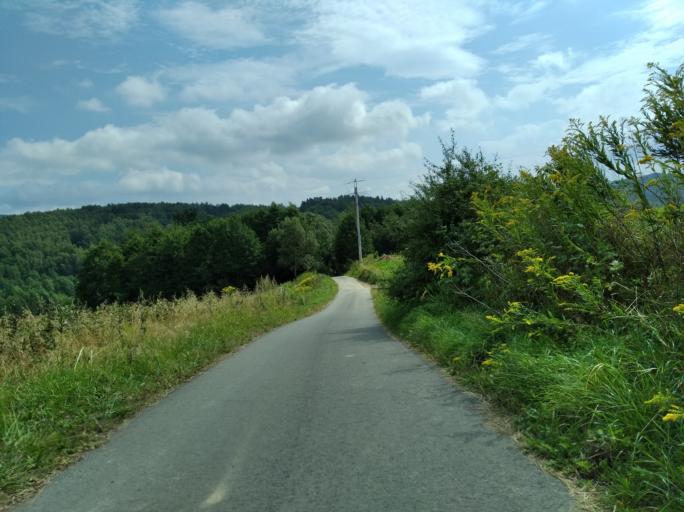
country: PL
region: Subcarpathian Voivodeship
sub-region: Powiat krosnienski
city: Leki
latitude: 49.8091
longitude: 21.6689
